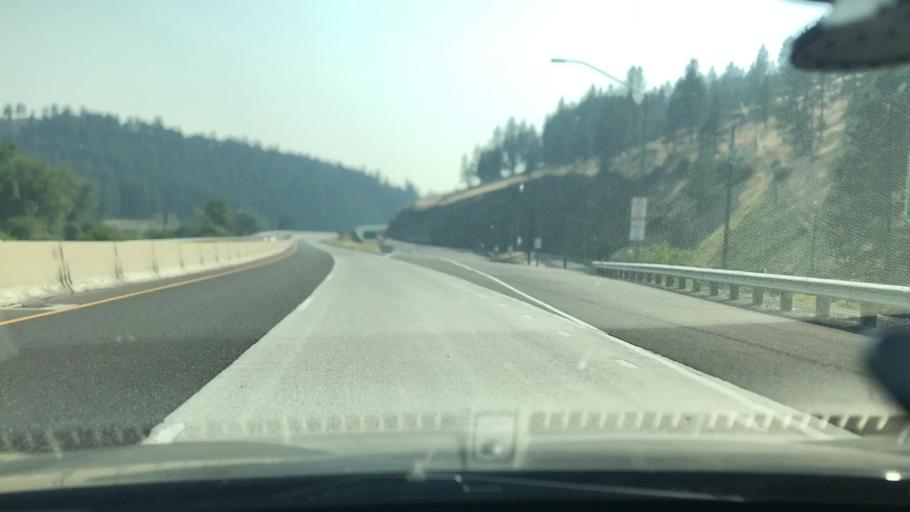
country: US
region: Oregon
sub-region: Union County
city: La Grande
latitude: 45.3461
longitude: -118.2238
